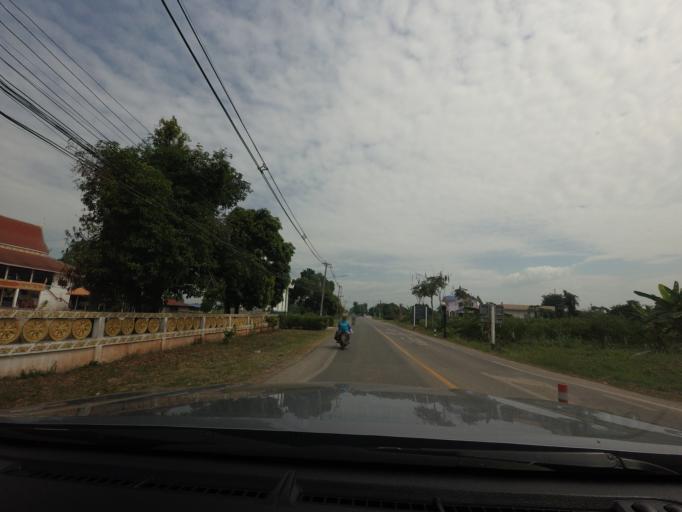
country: TH
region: Phitsanulok
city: Phitsanulok
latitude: 16.7174
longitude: 100.3199
